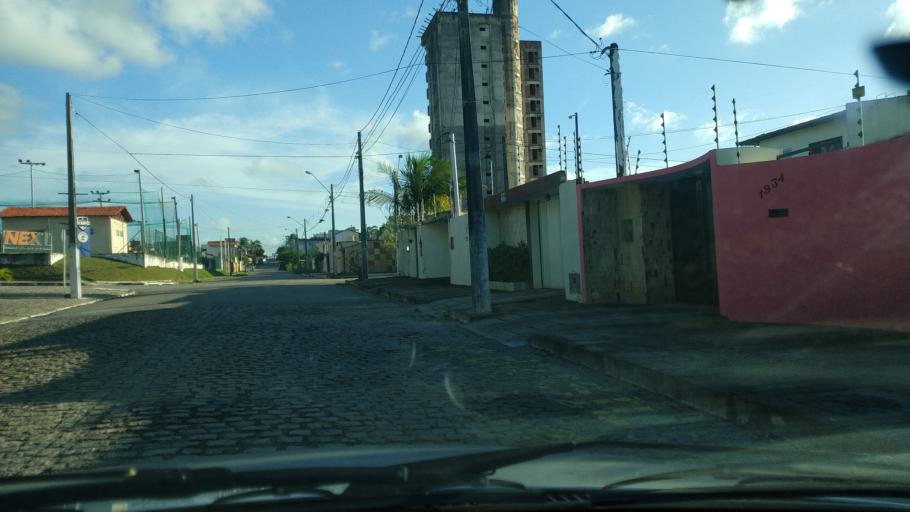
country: BR
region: Rio Grande do Norte
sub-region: Natal
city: Natal
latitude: -5.8644
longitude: -35.1969
